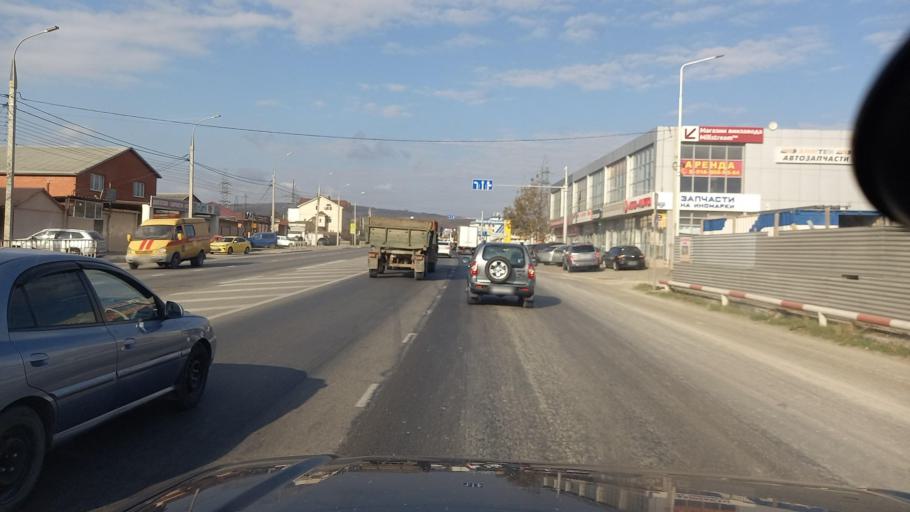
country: RU
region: Krasnodarskiy
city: Gayduk
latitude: 44.7668
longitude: 37.7103
